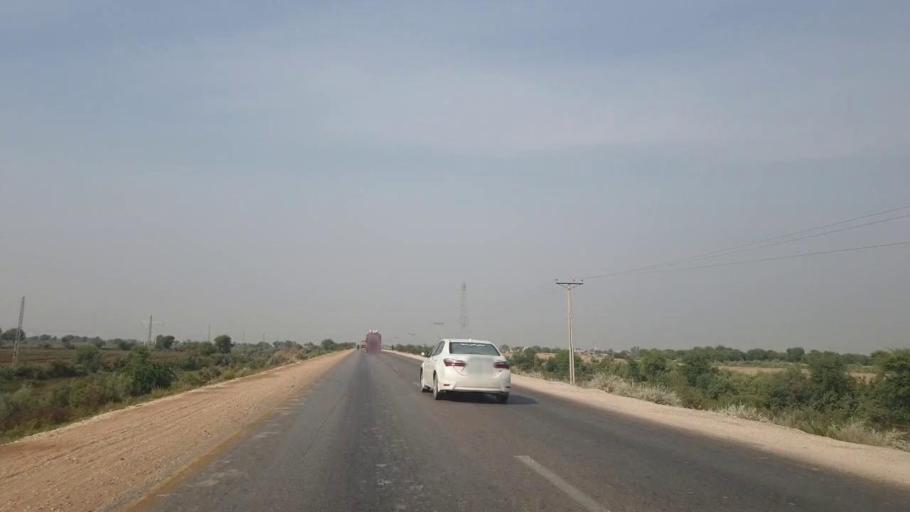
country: PK
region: Sindh
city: Sann
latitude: 26.0804
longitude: 68.0947
